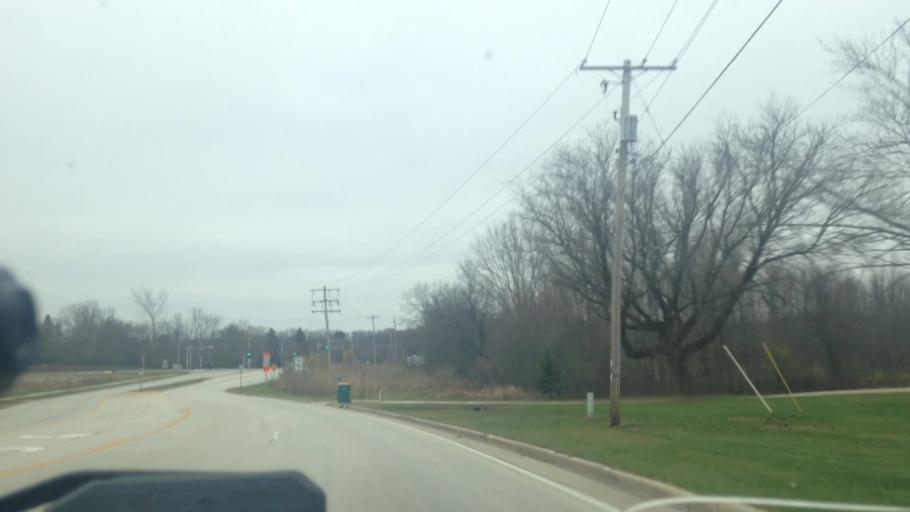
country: US
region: Wisconsin
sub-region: Waukesha County
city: Menomonee Falls
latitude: 43.1946
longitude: -88.1626
